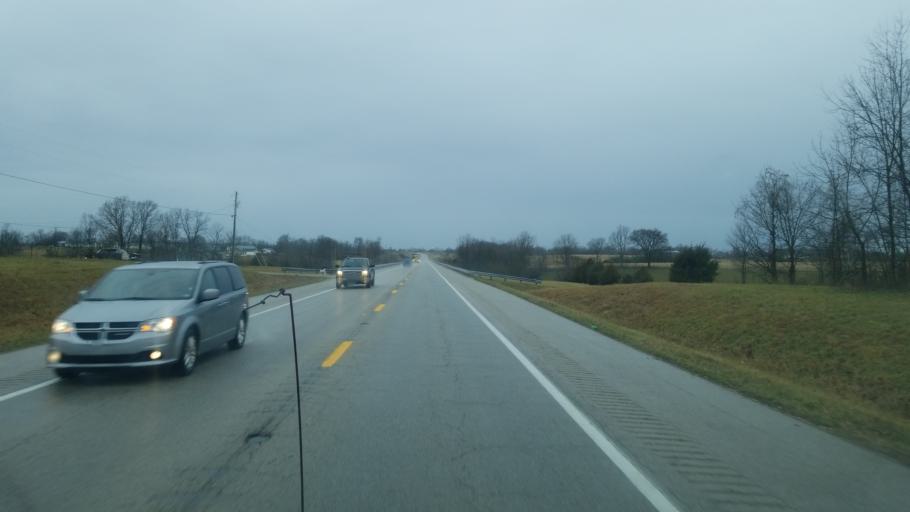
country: US
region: Ohio
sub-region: Adams County
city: Manchester
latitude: 38.5610
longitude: -83.6083
